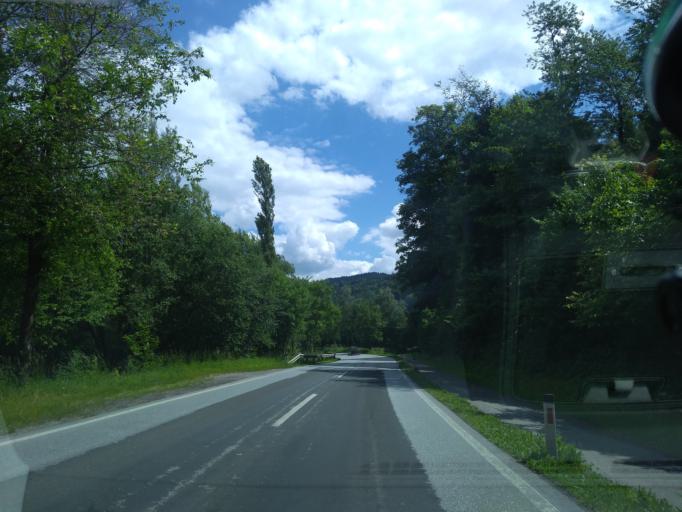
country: AT
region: Styria
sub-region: Politischer Bezirk Graz-Umgebung
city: Peggau
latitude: 47.1905
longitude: 15.3445
